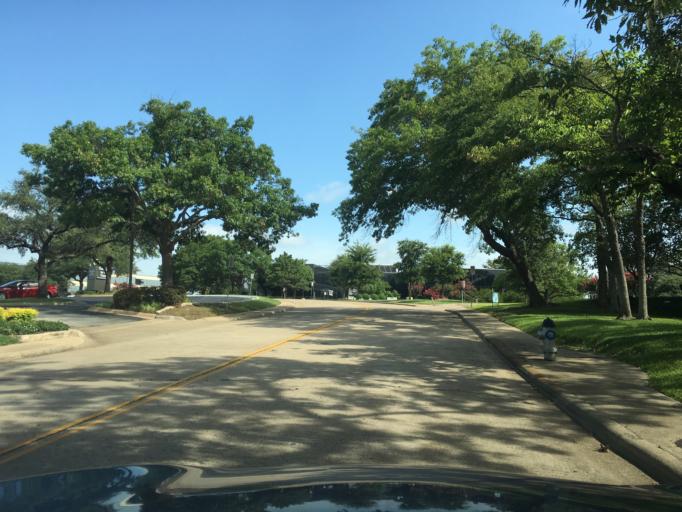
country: US
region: Texas
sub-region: Dallas County
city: Addison
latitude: 32.9225
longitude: -96.7880
